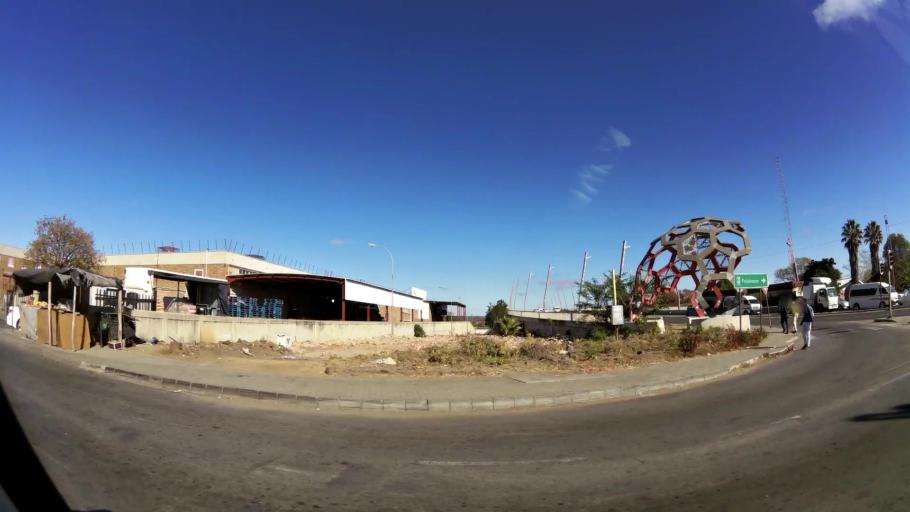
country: ZA
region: Limpopo
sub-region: Capricorn District Municipality
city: Polokwane
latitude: -23.8990
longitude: 29.4477
